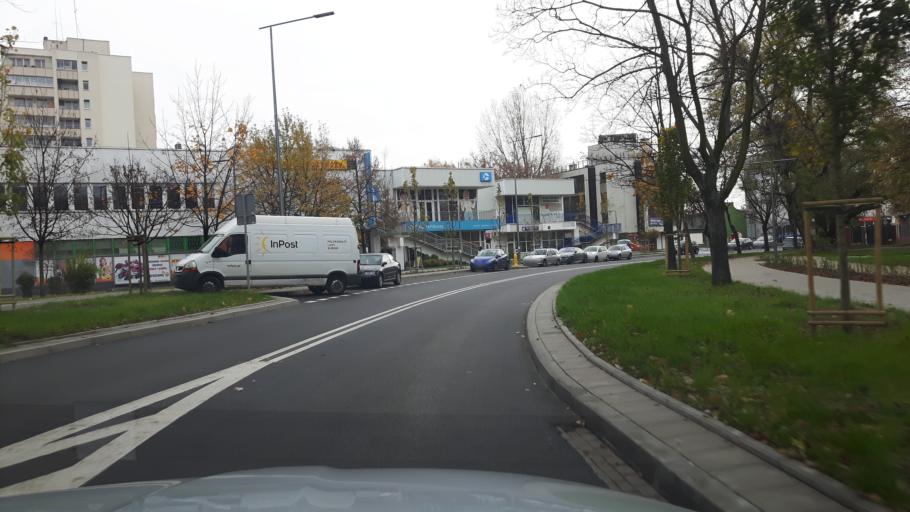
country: PL
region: Masovian Voivodeship
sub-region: Warszawa
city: Targowek
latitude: 52.2719
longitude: 21.0573
